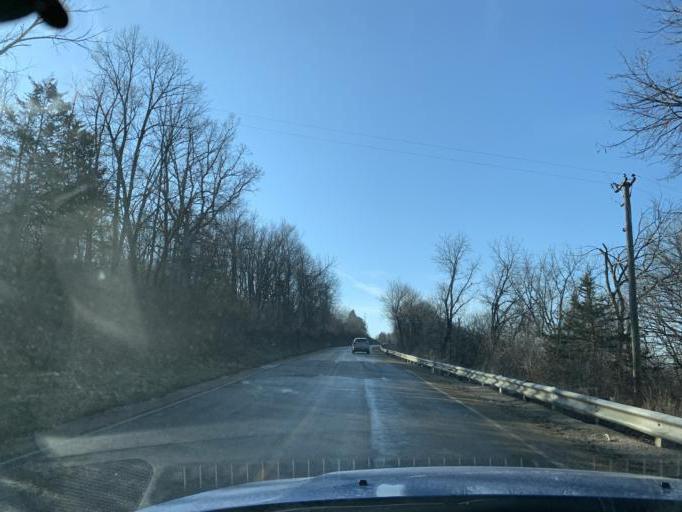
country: US
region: Wisconsin
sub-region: Iowa County
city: Barneveld
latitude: 42.8082
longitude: -89.8700
